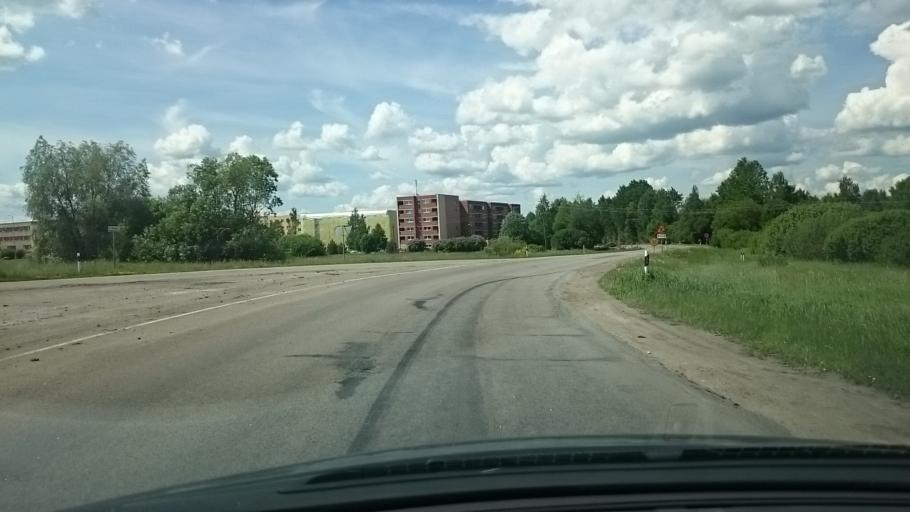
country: EE
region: Jaervamaa
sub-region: Paide linn
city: Paide
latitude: 58.8944
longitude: 25.5690
